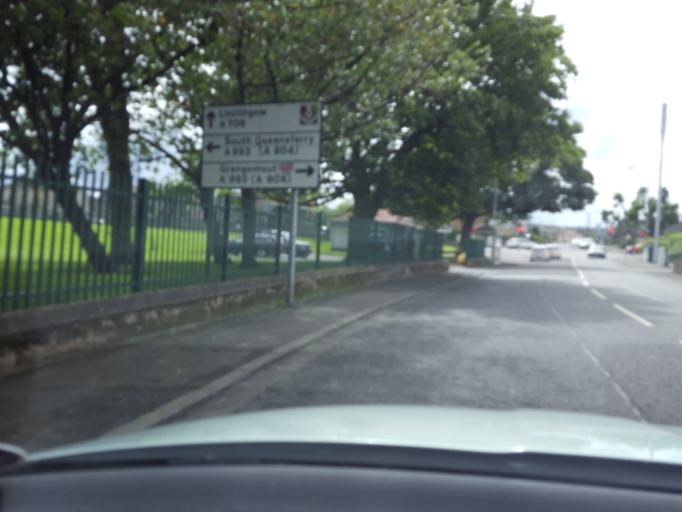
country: GB
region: Scotland
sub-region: Falkirk
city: Bo'ness
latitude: 56.0121
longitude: -3.6115
